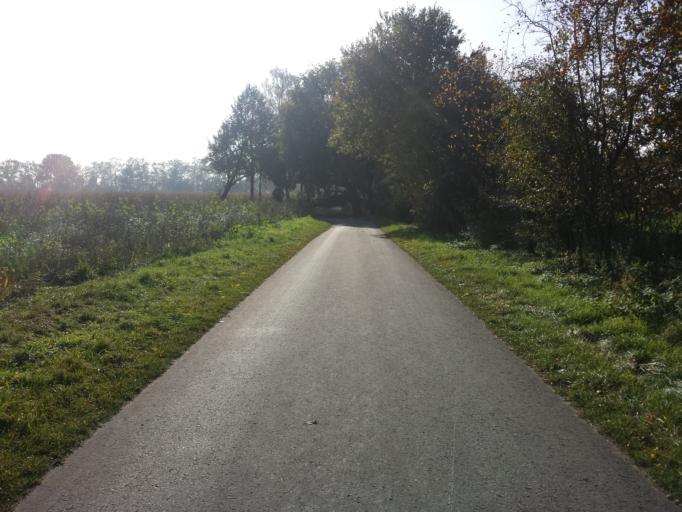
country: DE
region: North Rhine-Westphalia
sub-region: Regierungsbezirk Detmold
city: Guetersloh
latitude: 51.9318
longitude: 8.3379
